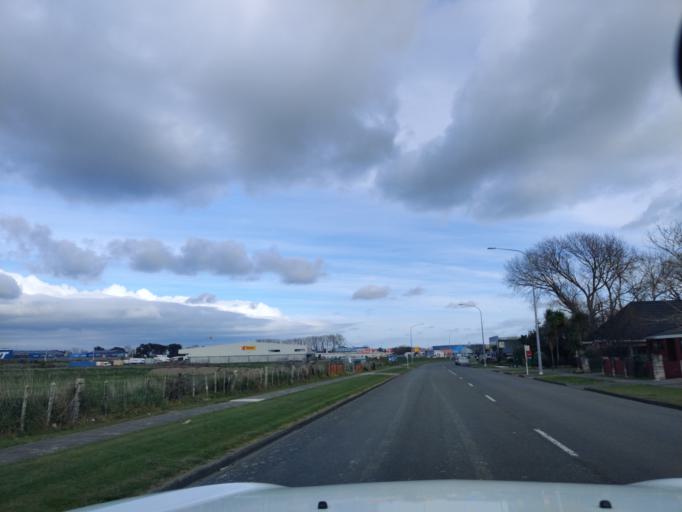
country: NZ
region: Manawatu-Wanganui
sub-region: Palmerston North City
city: Palmerston North
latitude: -40.3374
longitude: 175.6039
